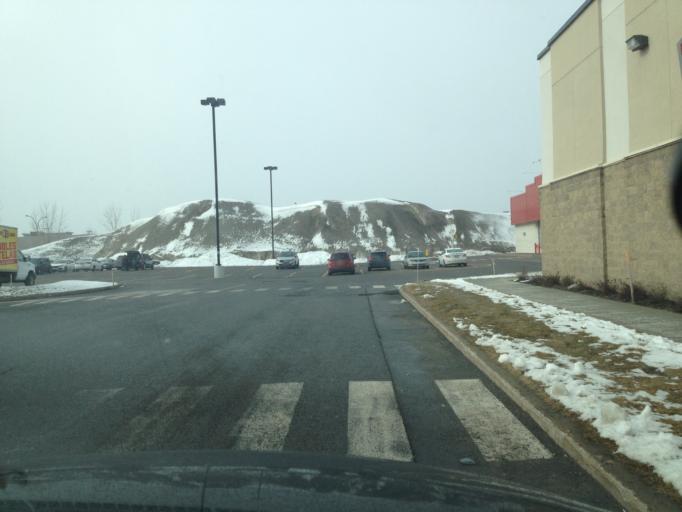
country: CA
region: Quebec
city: Dollard-Des Ormeaux
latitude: 45.5292
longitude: -73.7846
